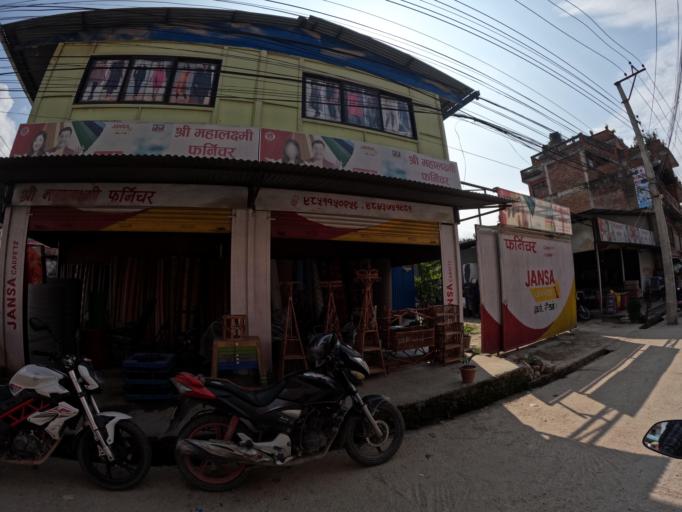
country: NP
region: Central Region
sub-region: Bagmati Zone
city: Bhaktapur
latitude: 27.6786
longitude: 85.4422
